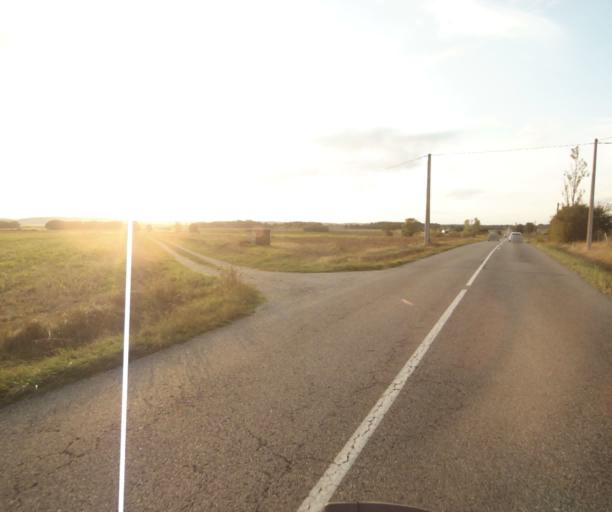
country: FR
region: Midi-Pyrenees
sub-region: Departement du Tarn-et-Garonne
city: Verdun-sur-Garonne
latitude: 43.8244
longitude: 1.1769
